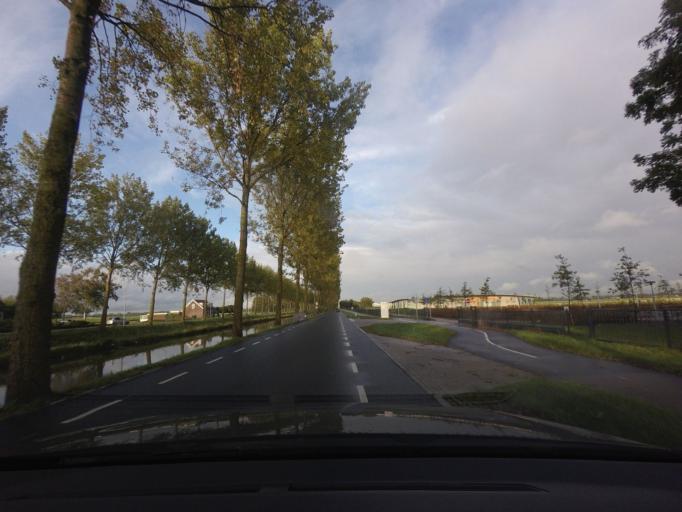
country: NL
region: North Holland
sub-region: Gemeente Haarlemmermeer
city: Hoofddorp
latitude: 52.2756
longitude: 4.6500
